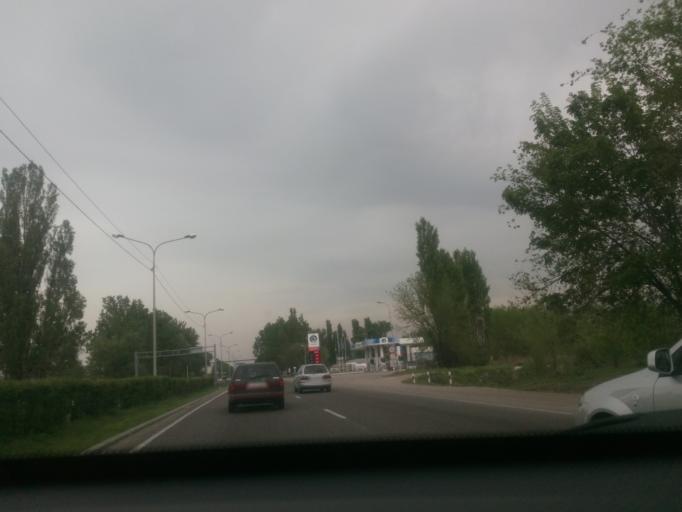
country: KZ
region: Almaty Oblysy
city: Burunday
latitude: 43.2265
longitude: 76.7397
